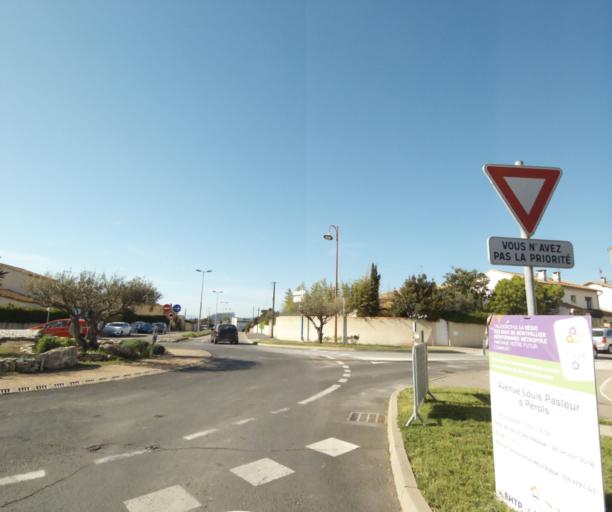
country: FR
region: Languedoc-Roussillon
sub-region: Departement de l'Herault
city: Perols
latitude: 43.5698
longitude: 3.9440
